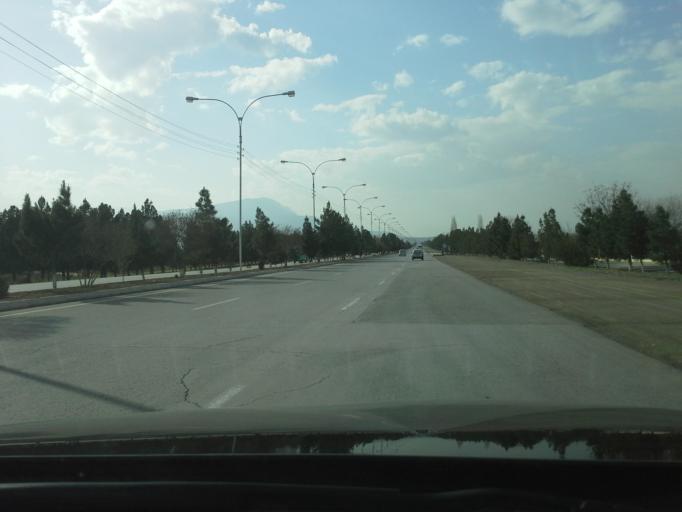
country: TM
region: Ahal
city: Abadan
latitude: 37.9728
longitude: 58.2579
